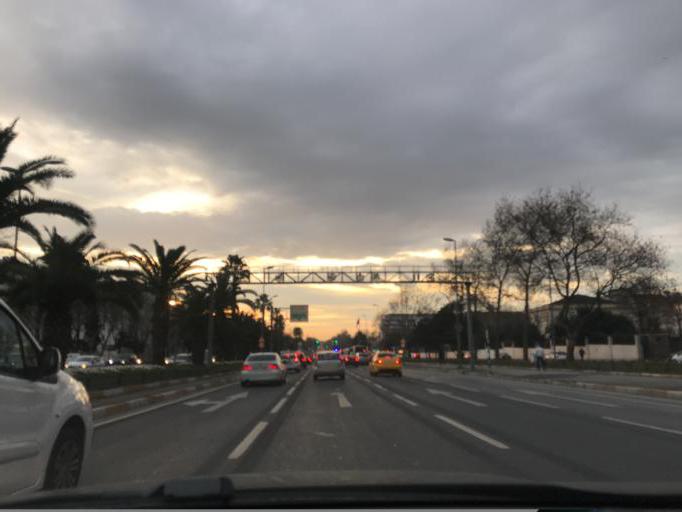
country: TR
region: Istanbul
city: Istanbul
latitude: 41.0228
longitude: 28.9317
